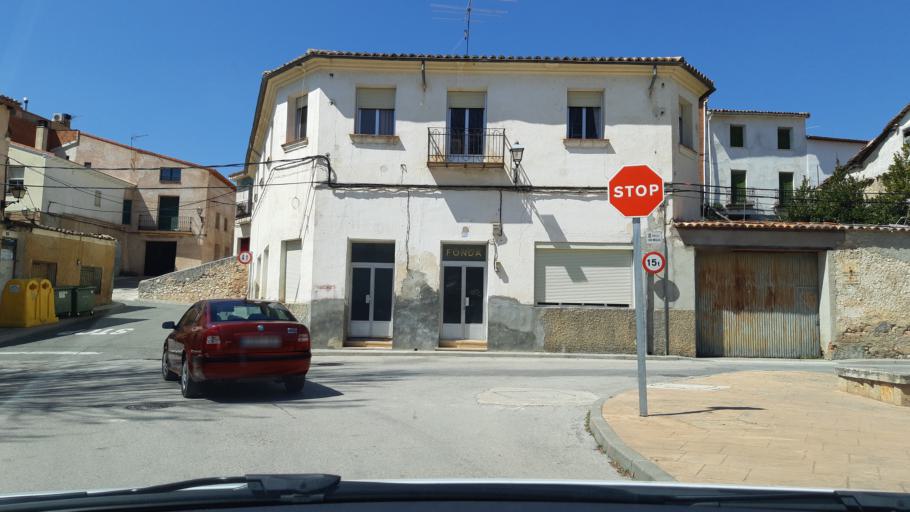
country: ES
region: Castille-La Mancha
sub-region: Provincia de Guadalajara
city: Cifuentes
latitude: 40.7839
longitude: -2.6227
